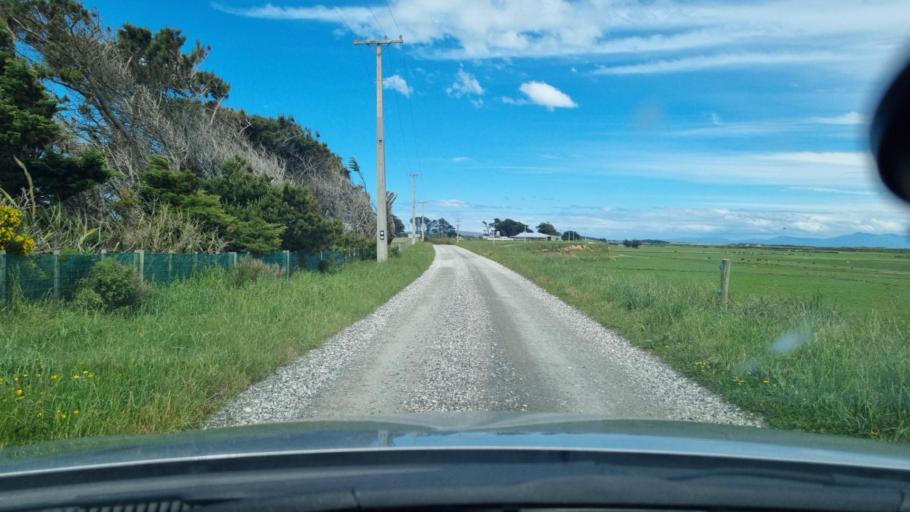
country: NZ
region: Southland
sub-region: Invercargill City
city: Invercargill
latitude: -46.3956
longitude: 168.2577
